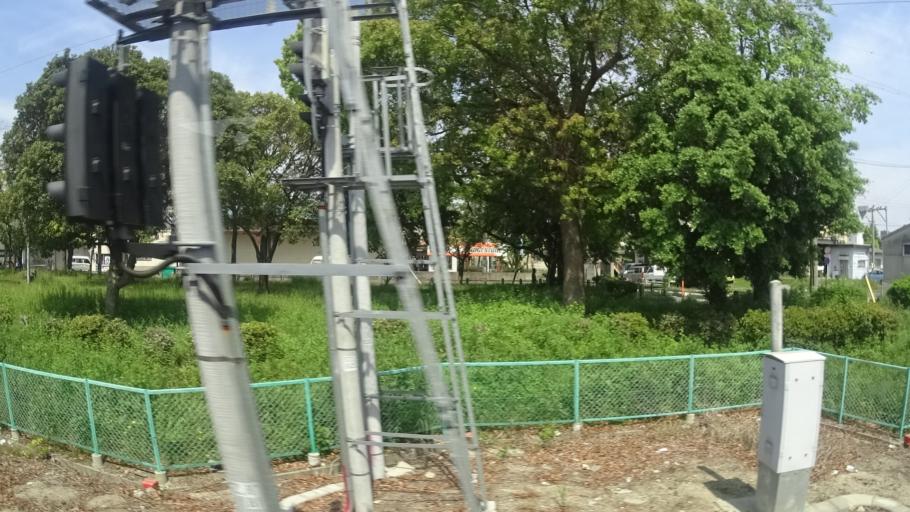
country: JP
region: Mie
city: Yokkaichi
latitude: 34.9556
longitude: 136.6244
